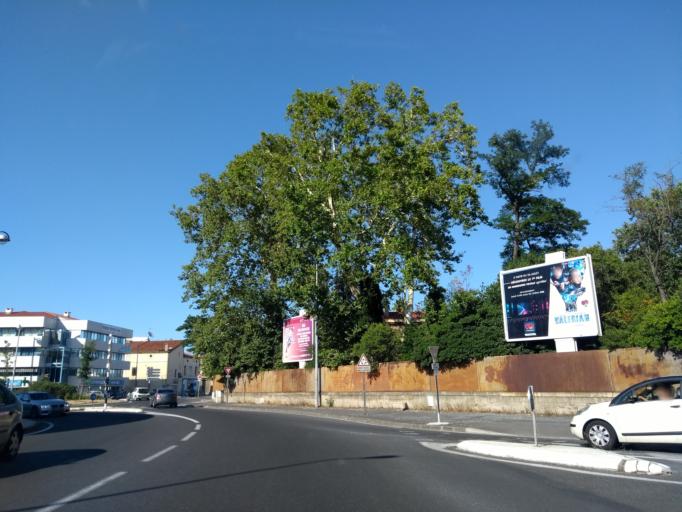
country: FR
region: Languedoc-Roussillon
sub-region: Departement des Pyrenees-Orientales
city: Perpignan
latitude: 42.6872
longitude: 2.9081
